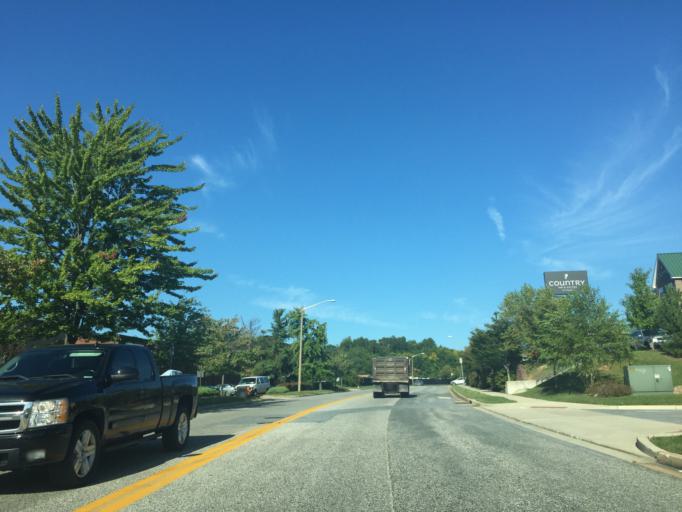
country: US
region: Maryland
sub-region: Baltimore County
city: Rossville
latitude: 39.3394
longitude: -76.4825
